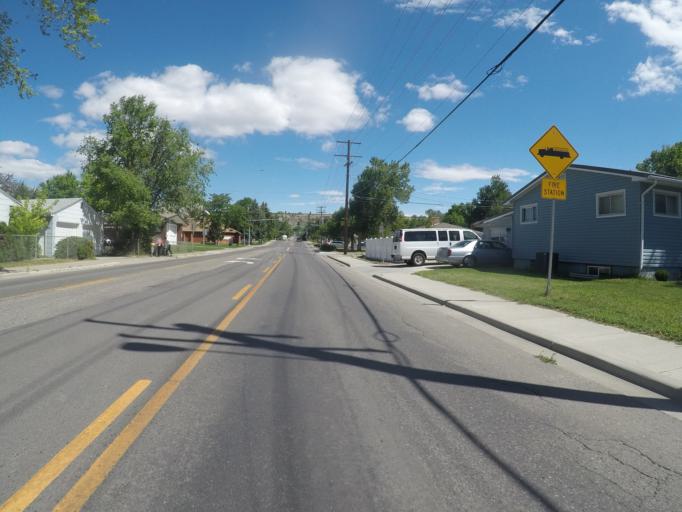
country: US
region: Montana
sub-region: Yellowstone County
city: Billings
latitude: 45.7891
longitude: -108.5590
